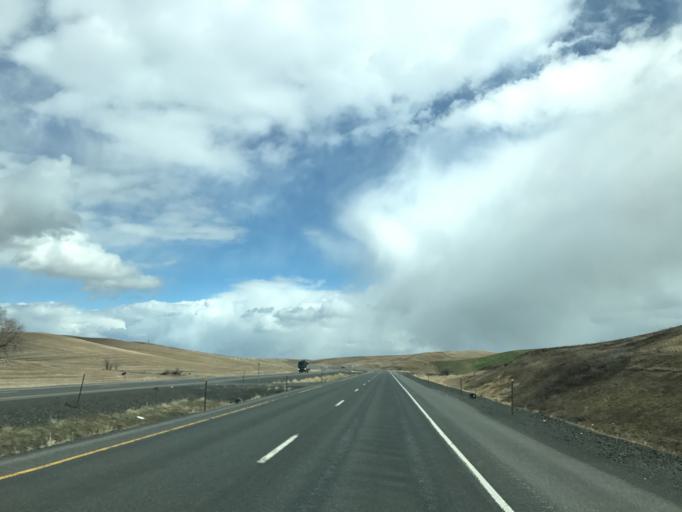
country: US
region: Idaho
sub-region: Nez Perce County
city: Lewiston
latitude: 46.5091
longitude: -116.9712
